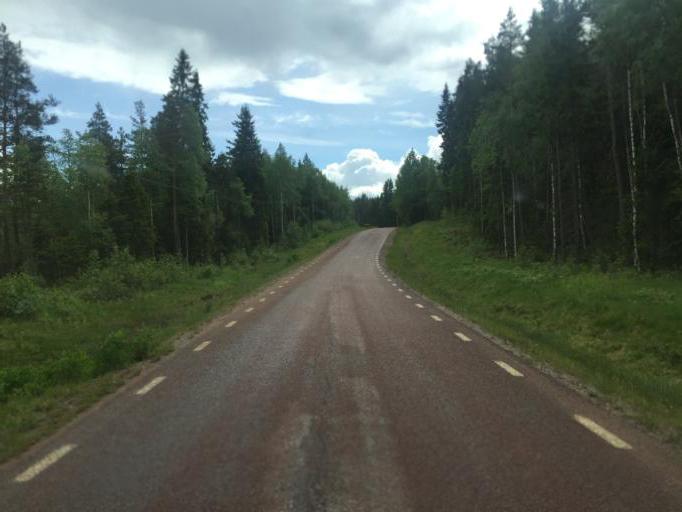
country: SE
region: Vaermland
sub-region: Hagfors Kommun
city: Hagfors
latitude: 60.3280
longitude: 13.8610
